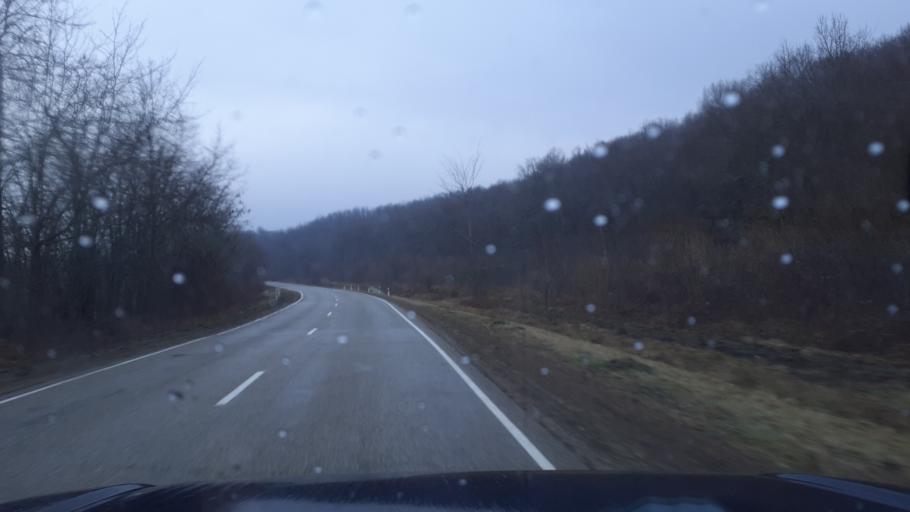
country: RU
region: Krasnodarskiy
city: Neftegorsk
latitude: 44.3185
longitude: 39.8330
